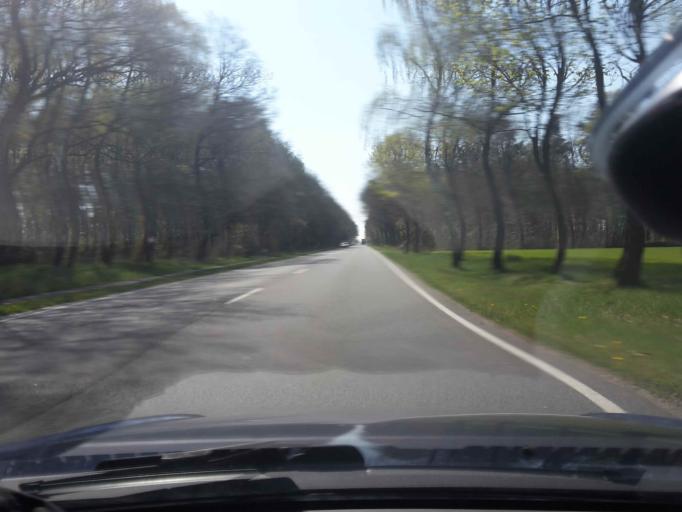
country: DE
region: Lower Saxony
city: Schneverdingen
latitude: 53.0957
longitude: 9.8579
